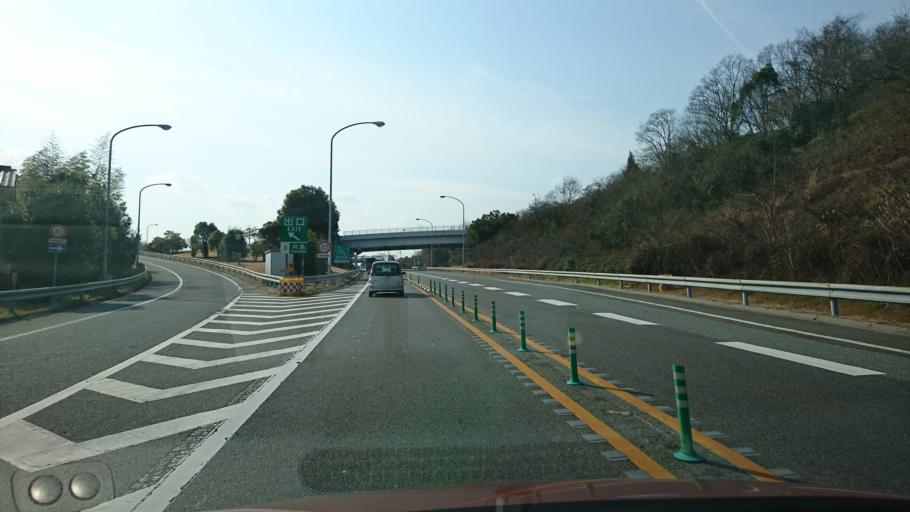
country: JP
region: Hiroshima
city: Onomichi
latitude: 34.3824
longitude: 133.1945
